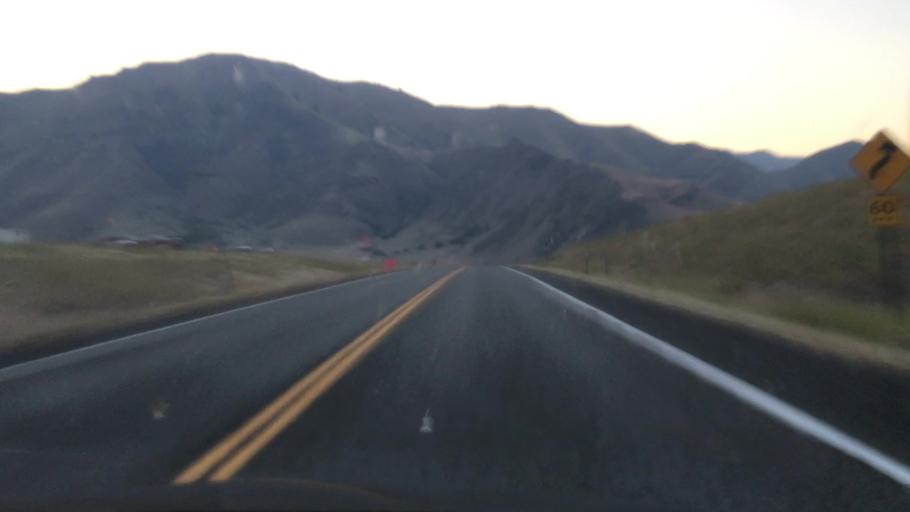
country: US
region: Idaho
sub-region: Idaho County
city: Grangeville
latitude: 45.6733
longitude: -116.3066
